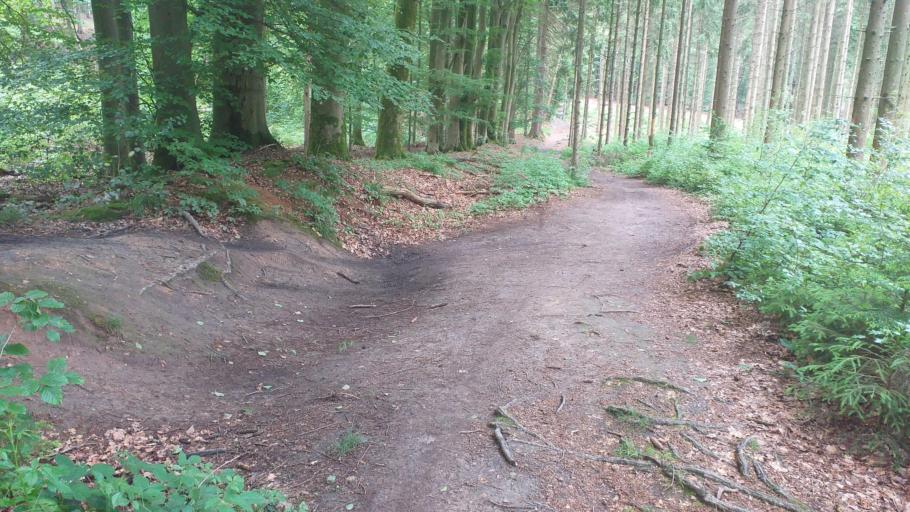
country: BE
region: Wallonia
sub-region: Province de Liege
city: La Calamine
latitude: 50.7239
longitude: 6.0597
